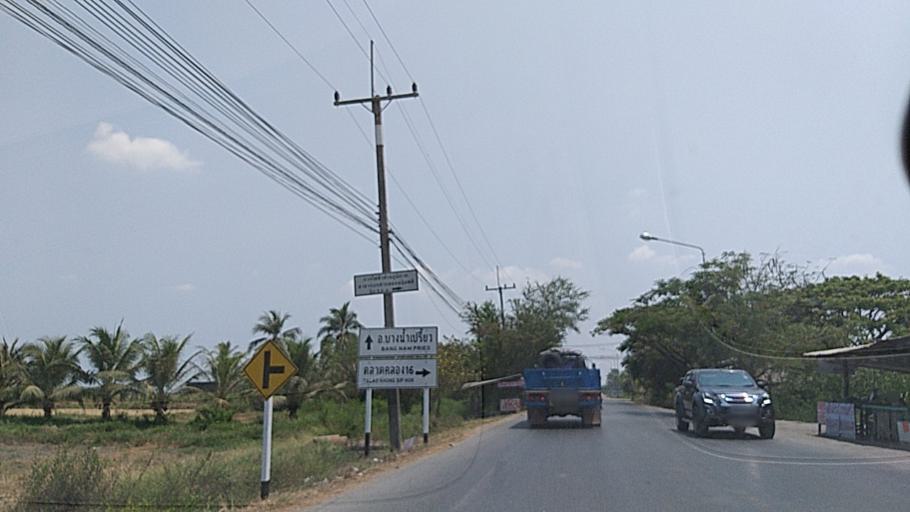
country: TH
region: Chachoengsao
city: Bang Nam Priao
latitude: 13.9717
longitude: 100.9652
